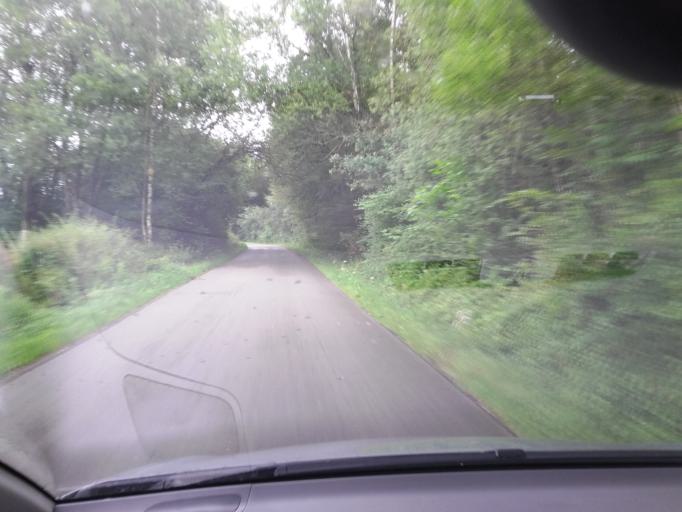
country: BE
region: Wallonia
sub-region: Province du Luxembourg
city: Attert
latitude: 49.7224
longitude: 5.8104
